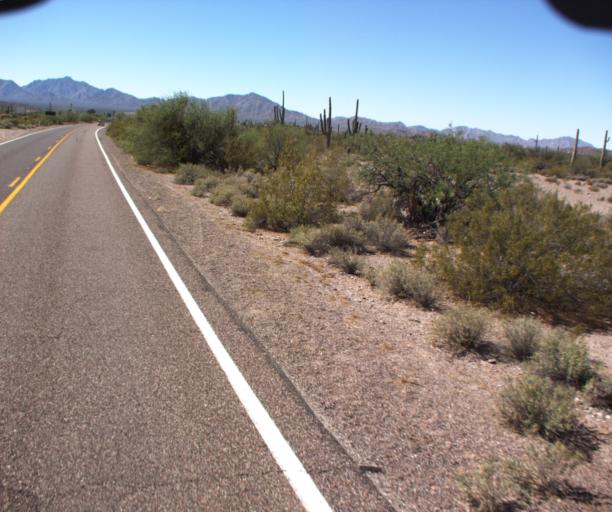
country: MX
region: Sonora
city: Sonoyta
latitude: 31.8904
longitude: -112.8124
